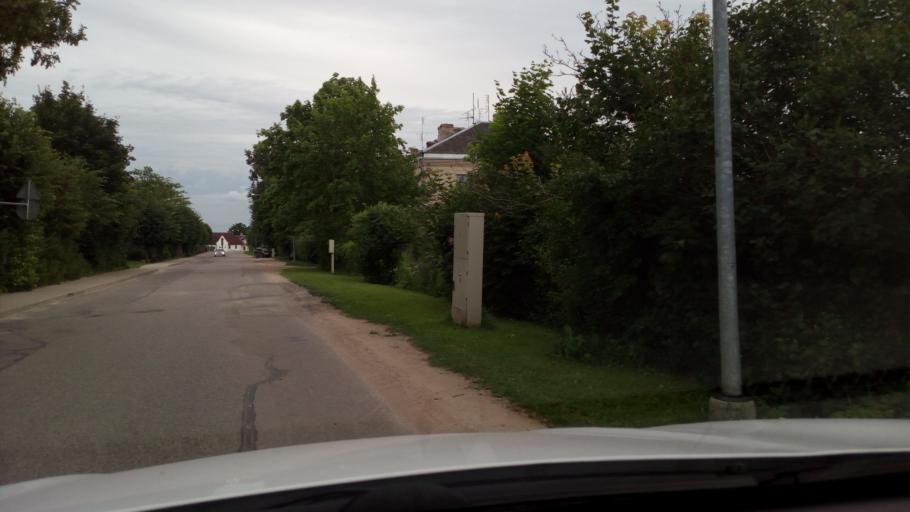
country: LV
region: Kandava
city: Kandava
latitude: 57.0416
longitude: 22.7746
